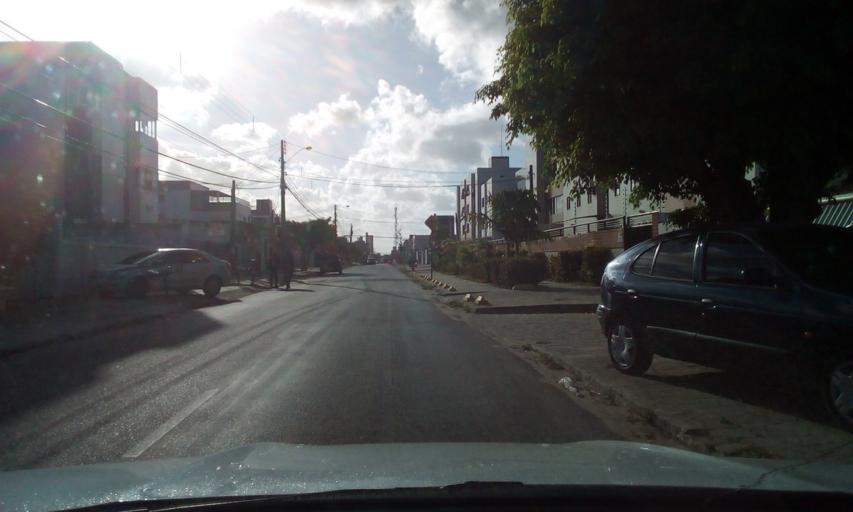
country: BR
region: Paraiba
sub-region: Joao Pessoa
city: Joao Pessoa
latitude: -7.1559
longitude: -34.8295
